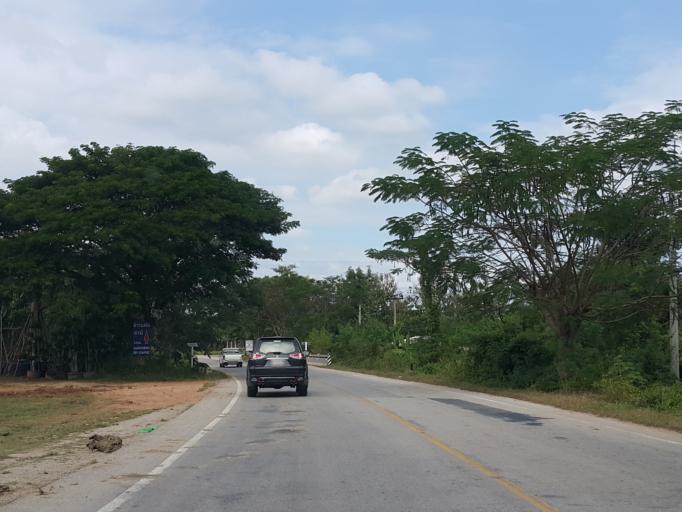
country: TH
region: Lampang
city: Lampang
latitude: 18.3635
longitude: 99.4585
